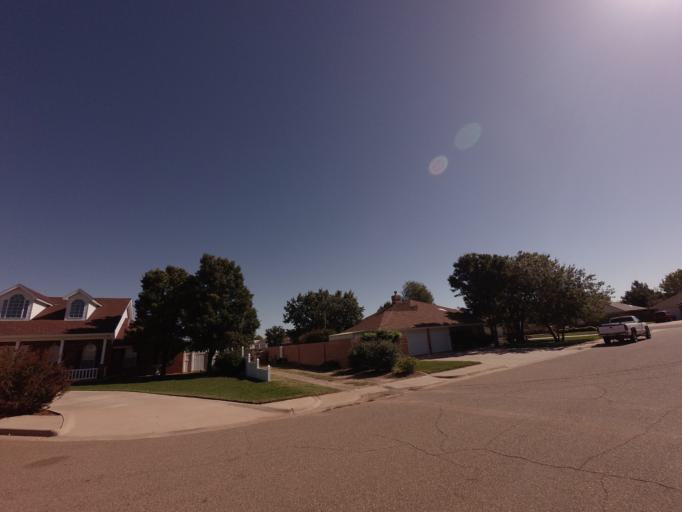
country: US
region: New Mexico
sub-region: Curry County
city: Clovis
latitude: 34.4261
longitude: -103.1742
